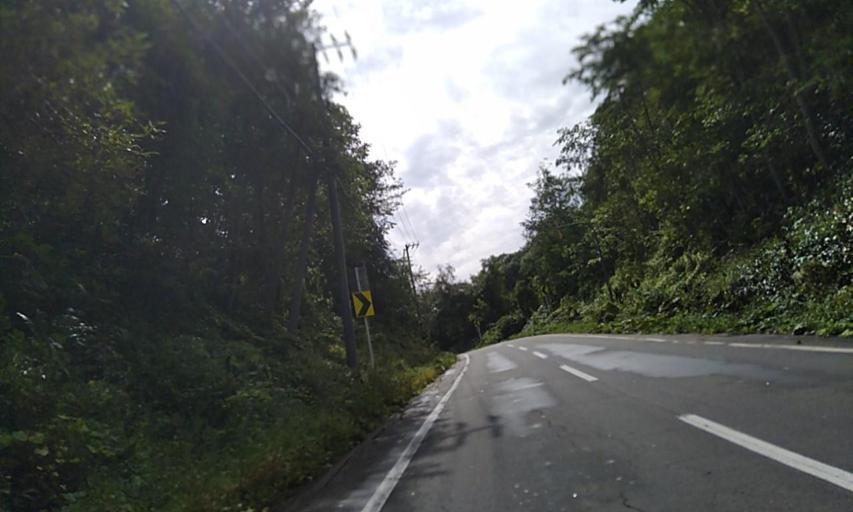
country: JP
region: Hokkaido
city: Kushiro
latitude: 42.8363
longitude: 143.8408
